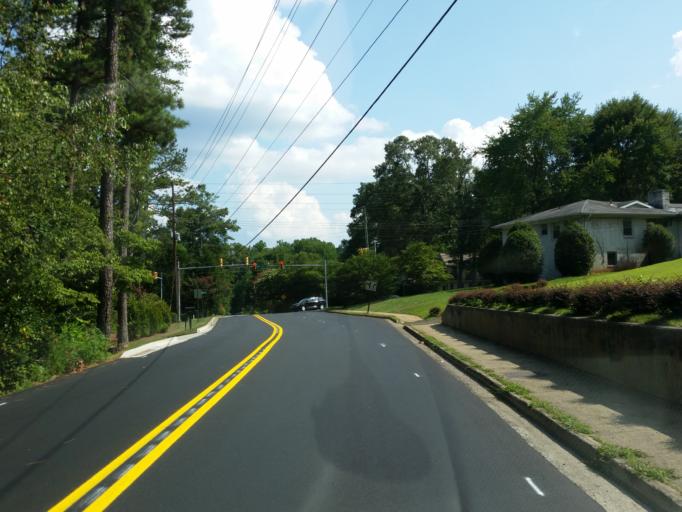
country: US
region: Georgia
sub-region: Cobb County
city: Marietta
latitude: 33.9861
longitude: -84.4590
